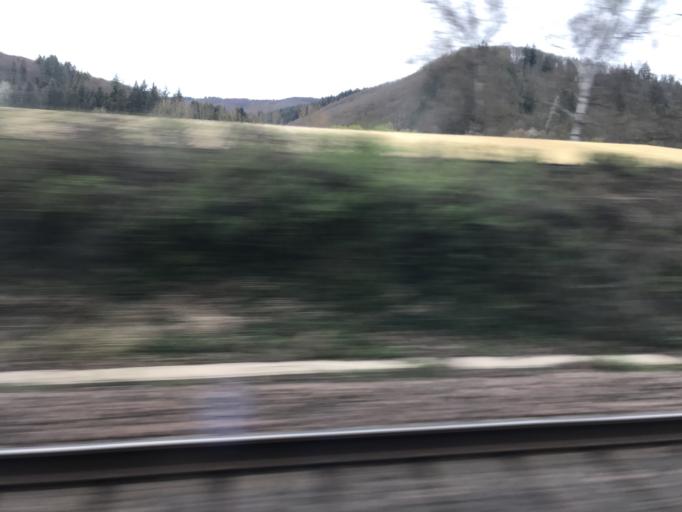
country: DE
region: Rheinland-Pfalz
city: Punderich
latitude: 50.0278
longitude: 7.0929
